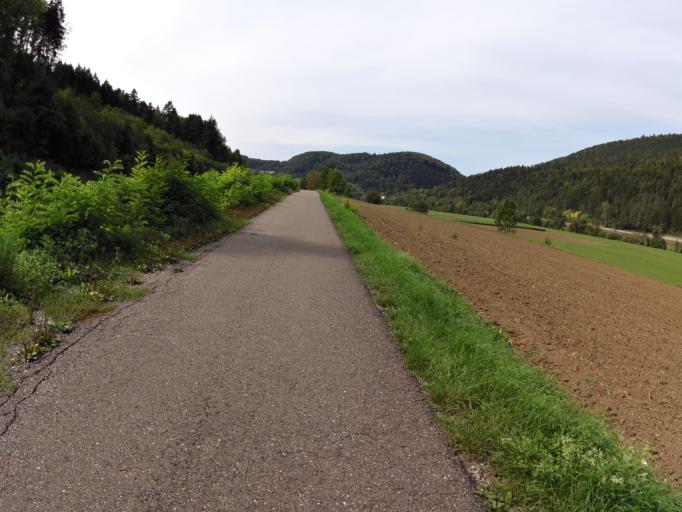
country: DE
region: Baden-Wuerttemberg
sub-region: Karlsruhe Region
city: Horb am Neckar
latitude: 48.4248
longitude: 8.6536
